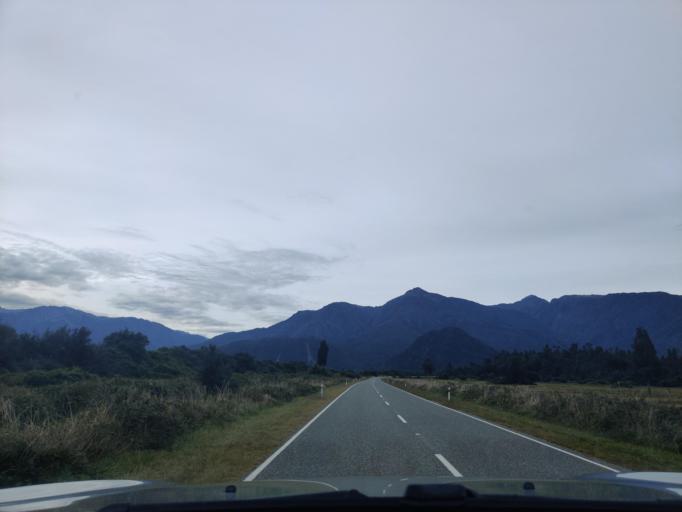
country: NZ
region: West Coast
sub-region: Westland District
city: Hokitika
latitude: -43.2660
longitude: 170.2940
